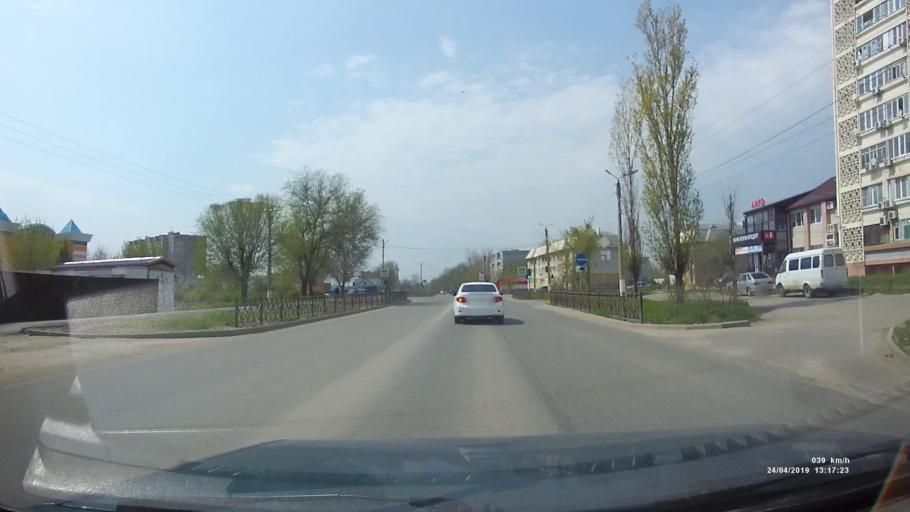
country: RU
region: Kalmykiya
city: Elista
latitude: 46.3054
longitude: 44.3003
